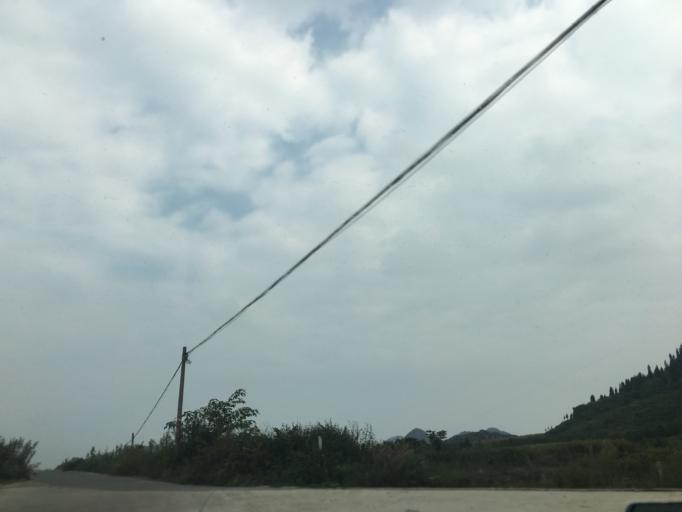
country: CN
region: Guangxi Zhuangzu Zizhiqu
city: Xinzhou
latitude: 25.4833
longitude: 105.6486
